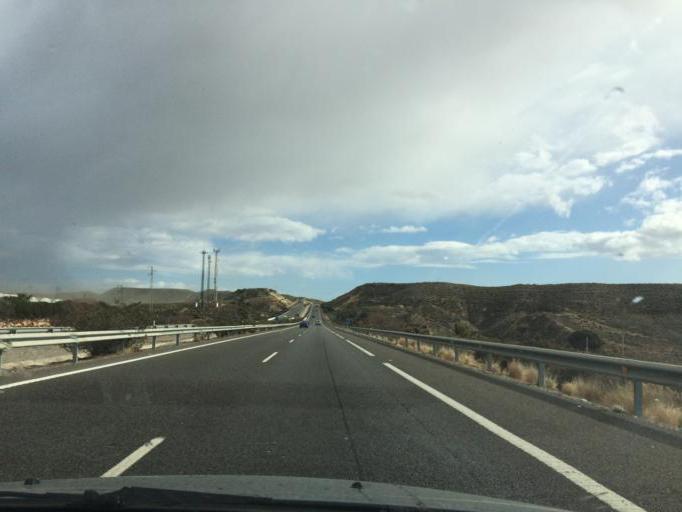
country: ES
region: Andalusia
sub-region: Provincia de Almeria
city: Retamar
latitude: 36.8702
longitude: -2.2997
